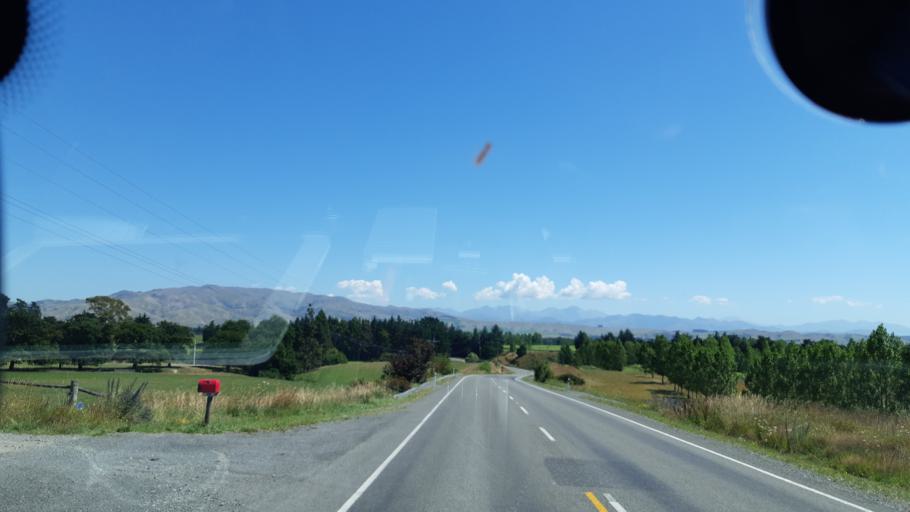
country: NZ
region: Canterbury
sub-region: Kaikoura District
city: Kaikoura
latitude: -42.7559
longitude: 173.2744
